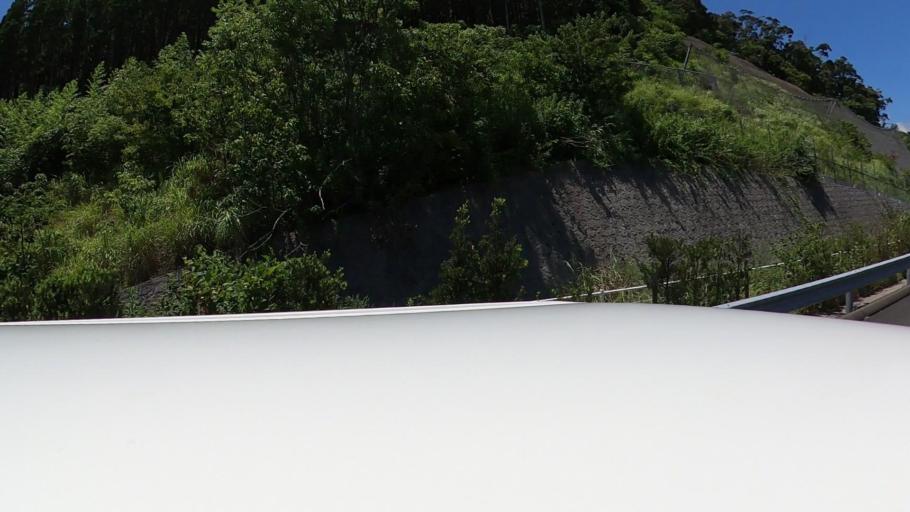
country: JP
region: Miyazaki
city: Nobeoka
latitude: 32.3943
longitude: 131.6212
